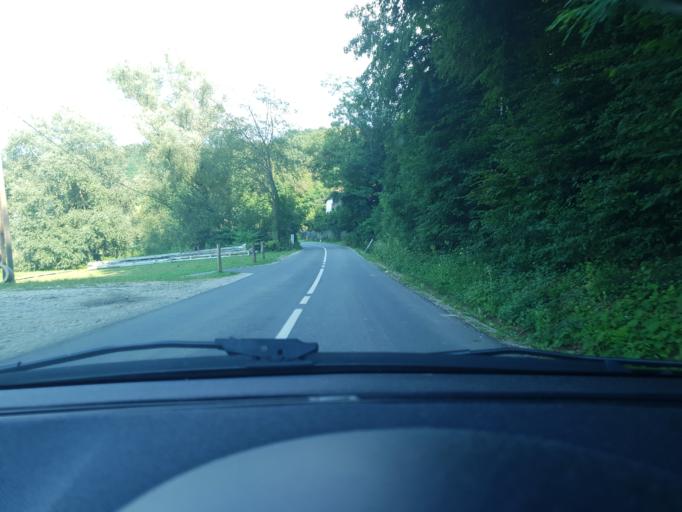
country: HR
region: Krapinsko-Zagorska
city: Pregrada
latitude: 46.0768
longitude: 15.7982
